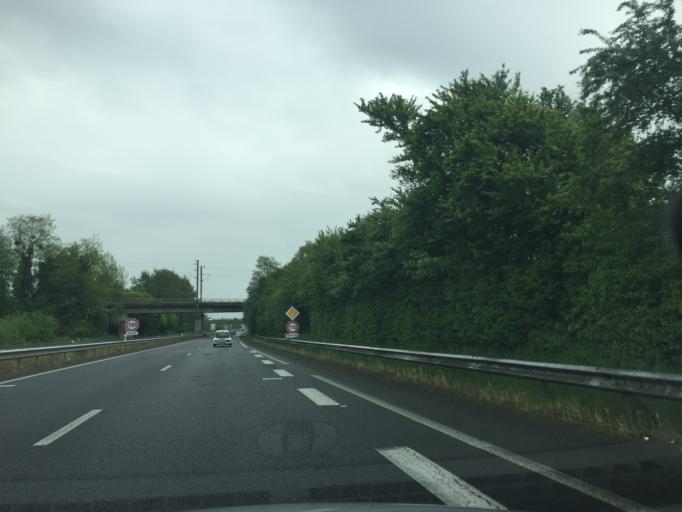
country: FR
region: Brittany
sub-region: Departement d'Ille-et-Vilaine
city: Dol-de-Bretagne
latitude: 48.5540
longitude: -1.7537
